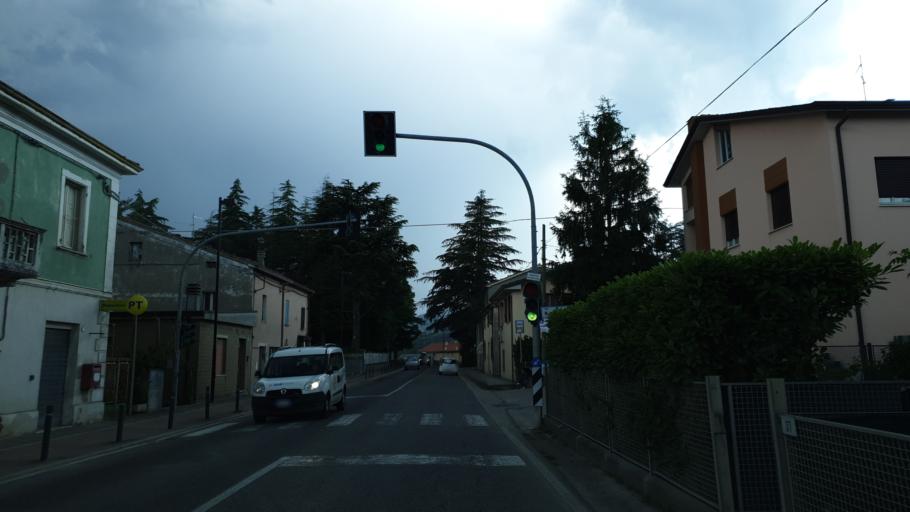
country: IT
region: Emilia-Romagna
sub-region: Provincia di Rimini
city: Secchiano
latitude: 43.9241
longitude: 12.3173
